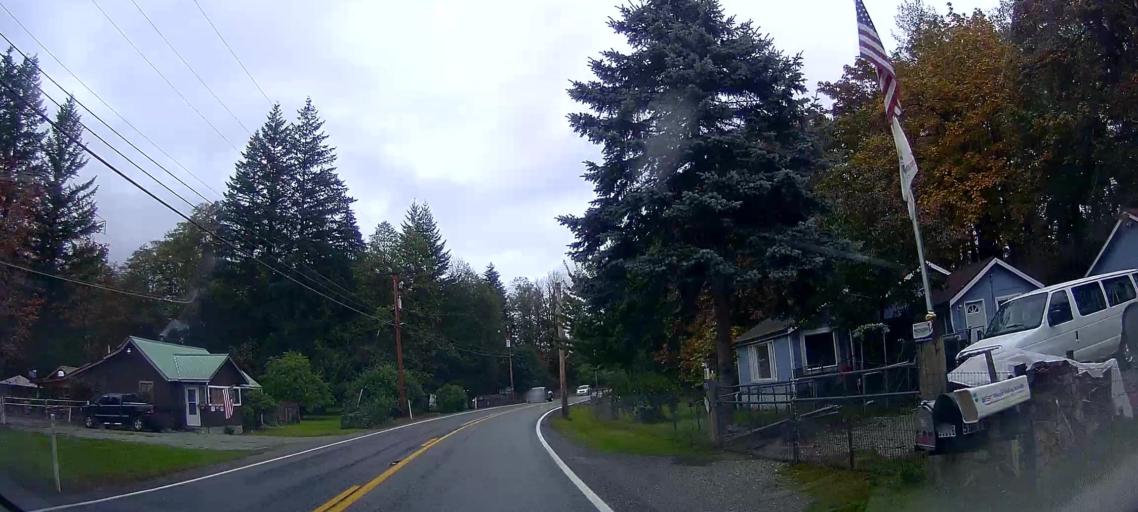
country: US
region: Washington
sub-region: Snohomish County
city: Darrington
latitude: 48.5240
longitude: -121.4591
